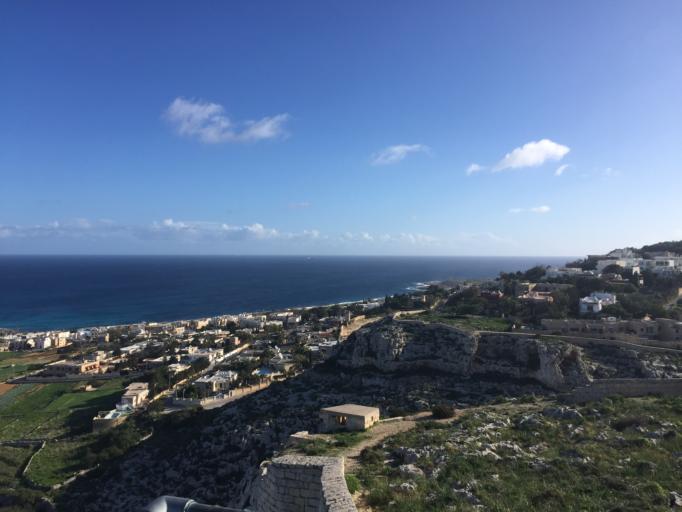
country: MT
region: Hal Gharghur
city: Hal Gharghur
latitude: 35.9318
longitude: 14.4537
